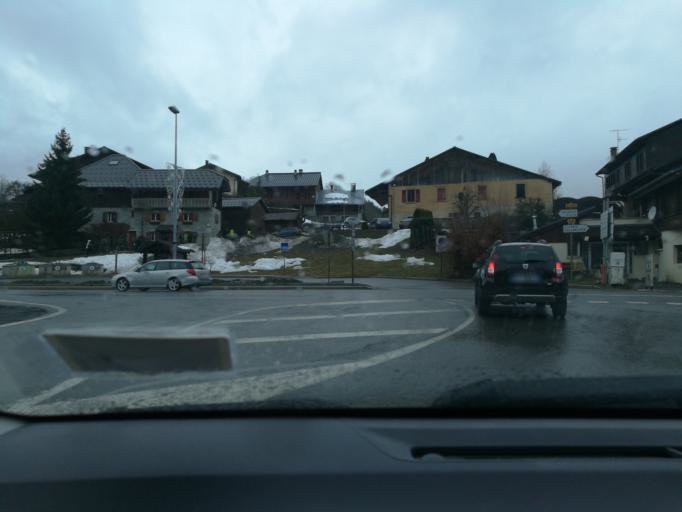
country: FR
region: Rhone-Alpes
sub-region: Departement de la Haute-Savoie
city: Araches-la-Frasse
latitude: 46.0436
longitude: 6.6324
